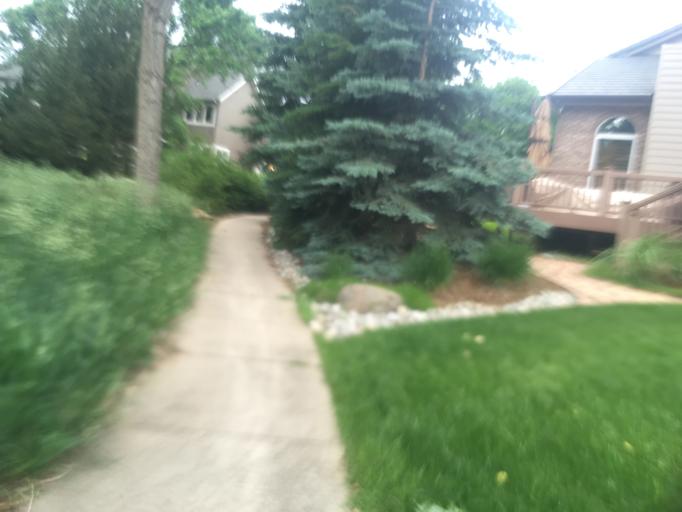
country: US
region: Colorado
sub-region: Boulder County
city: Superior
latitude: 39.9637
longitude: -105.1527
